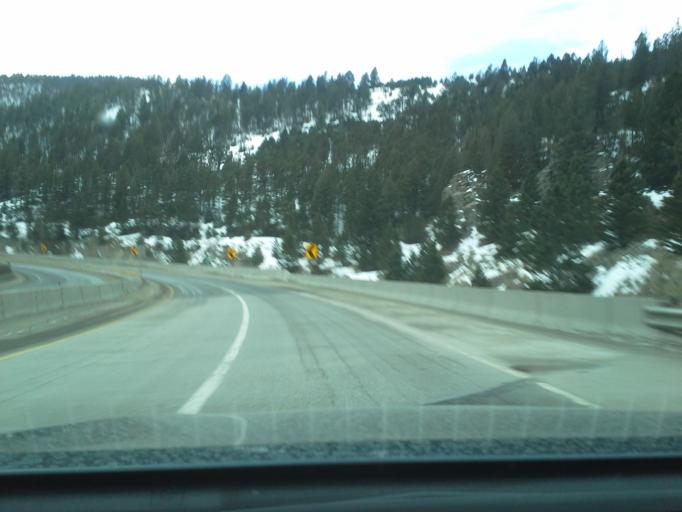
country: US
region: Montana
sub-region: Jefferson County
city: Boulder
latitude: 46.2683
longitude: -112.2848
